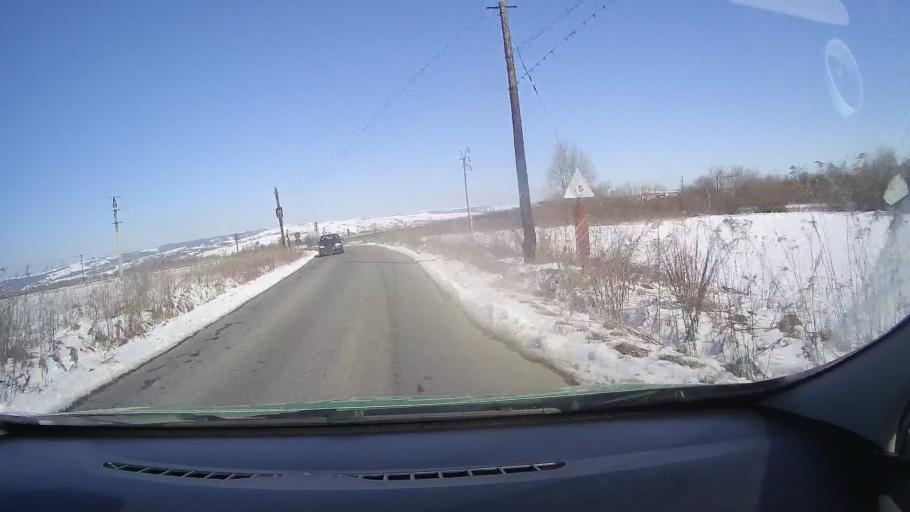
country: RO
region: Brasov
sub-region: Comuna Mandra
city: Mandra
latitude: 45.8299
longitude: 25.0130
